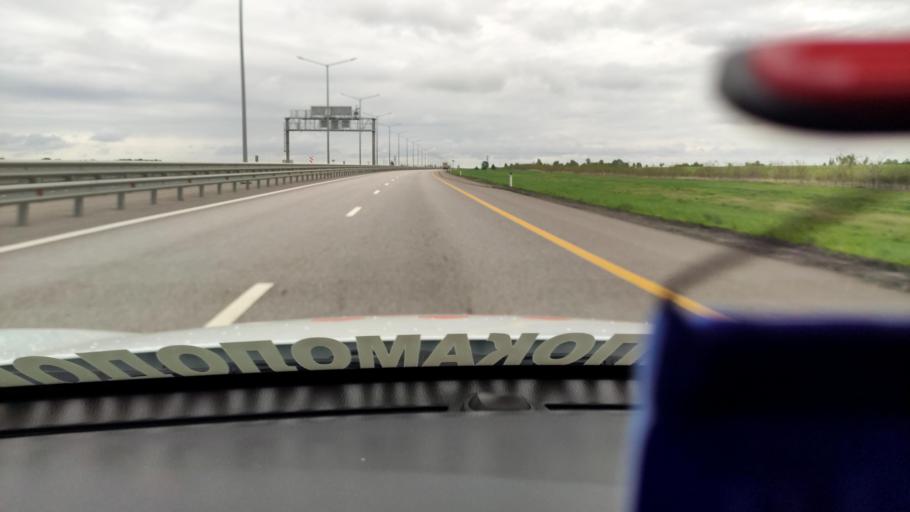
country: RU
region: Voronezj
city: Novaya Usman'
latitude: 51.6011
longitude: 39.3440
